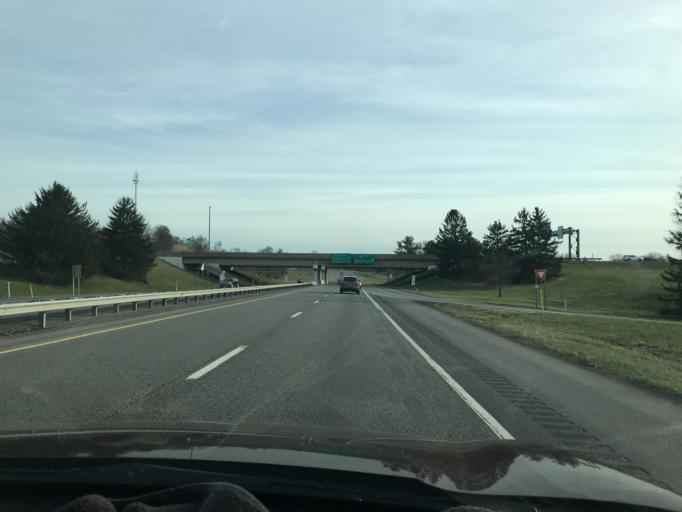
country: US
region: Pennsylvania
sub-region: Union County
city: New Columbia
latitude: 41.0515
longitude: -76.8394
